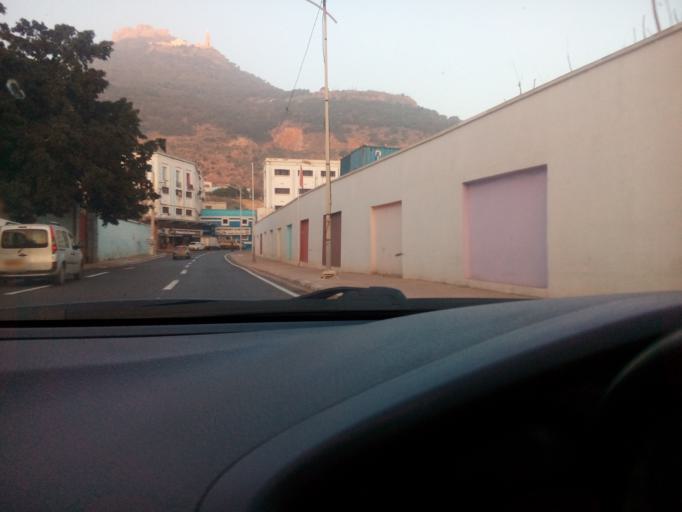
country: DZ
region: Oran
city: Oran
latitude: 35.7079
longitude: -0.6537
